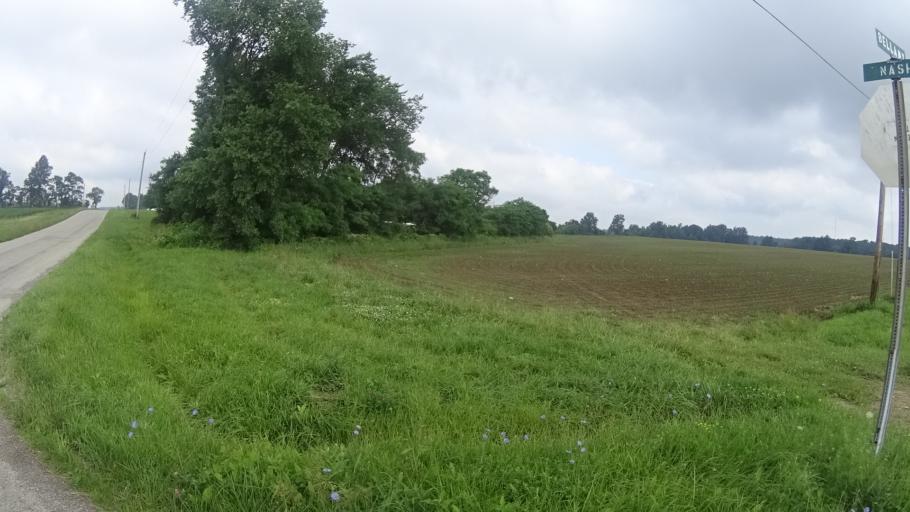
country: US
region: Ohio
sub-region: Huron County
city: Wakeman
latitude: 41.2846
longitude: -82.4808
